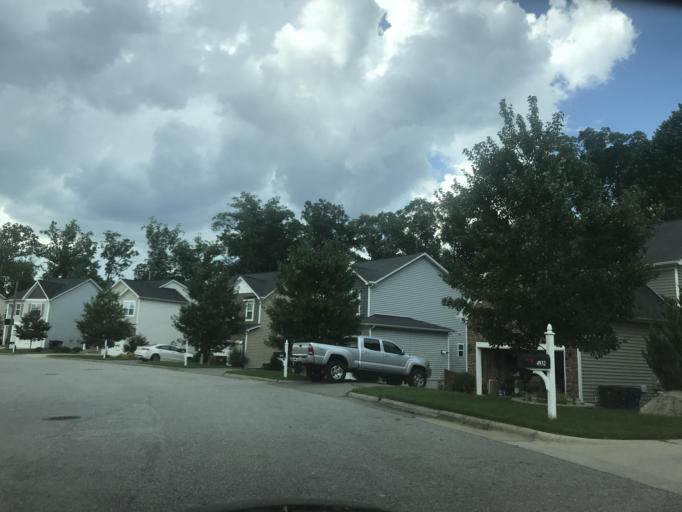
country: US
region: North Carolina
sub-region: Wake County
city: Knightdale
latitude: 35.8409
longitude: -78.5529
